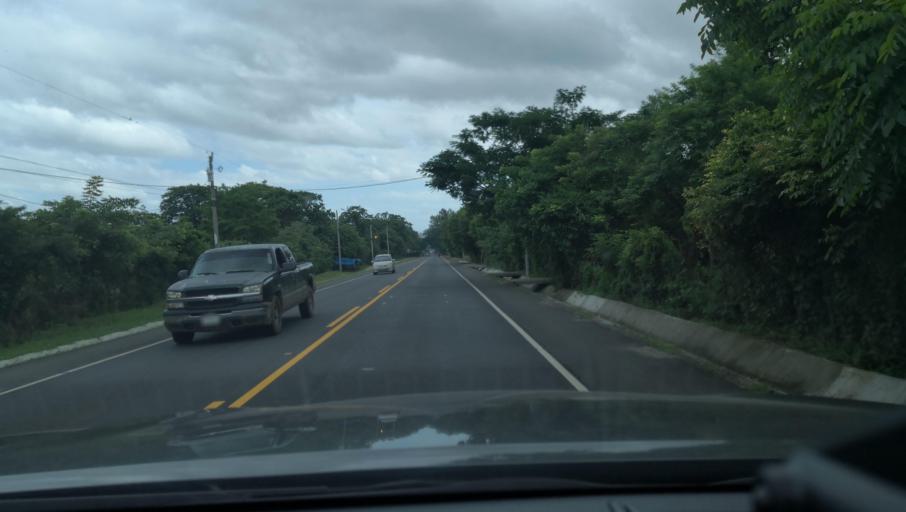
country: NI
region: Masaya
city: Nindiri
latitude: 12.0353
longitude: -86.1262
